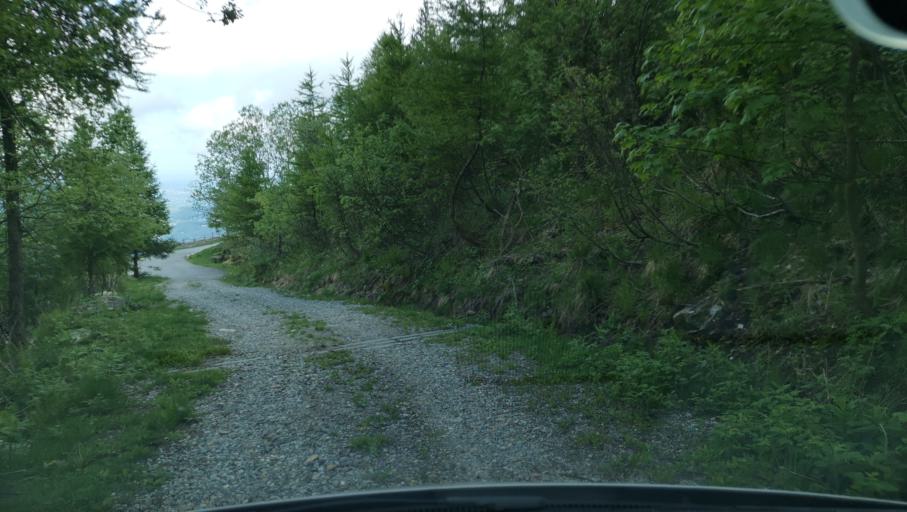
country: IT
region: Piedmont
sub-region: Provincia di Torino
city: Tavagnasco
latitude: 45.5346
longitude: 7.7963
